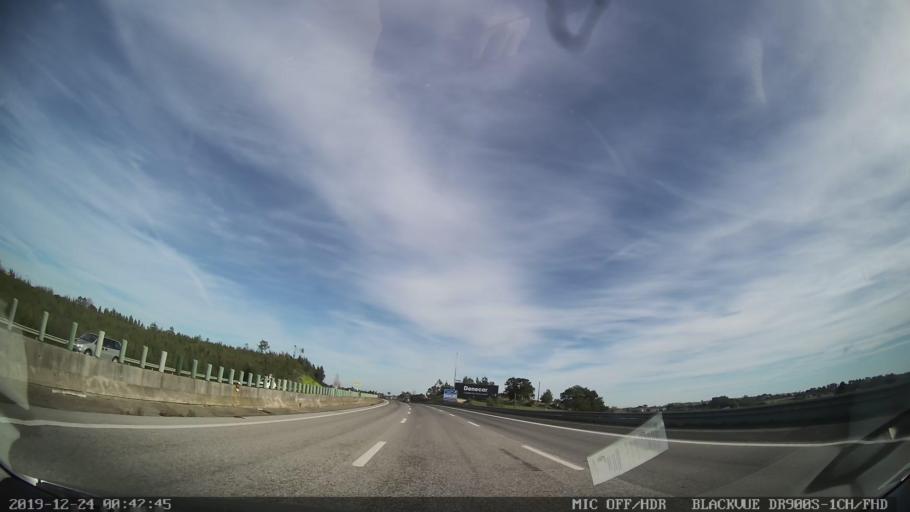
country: PT
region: Lisbon
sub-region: Azambuja
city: Aveiras de Cima
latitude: 39.1178
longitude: -8.9147
